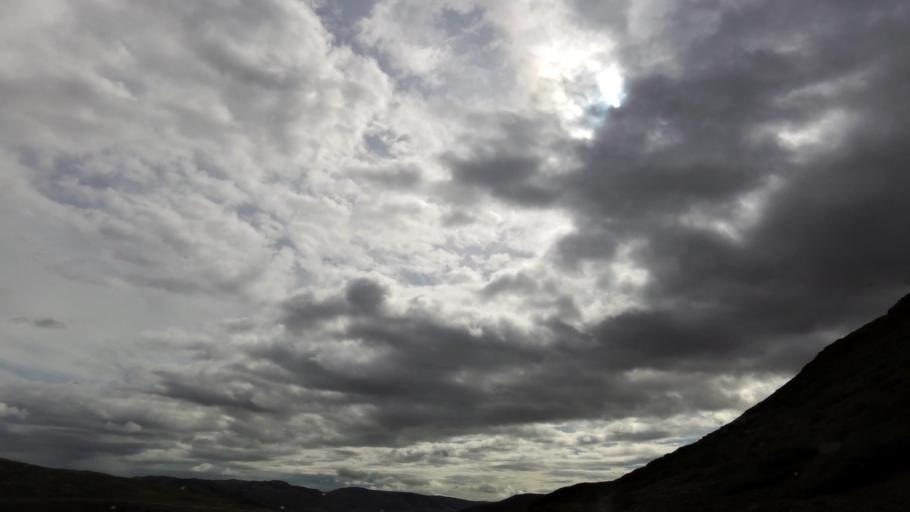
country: IS
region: West
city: Stykkisholmur
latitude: 65.5966
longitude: -22.1229
